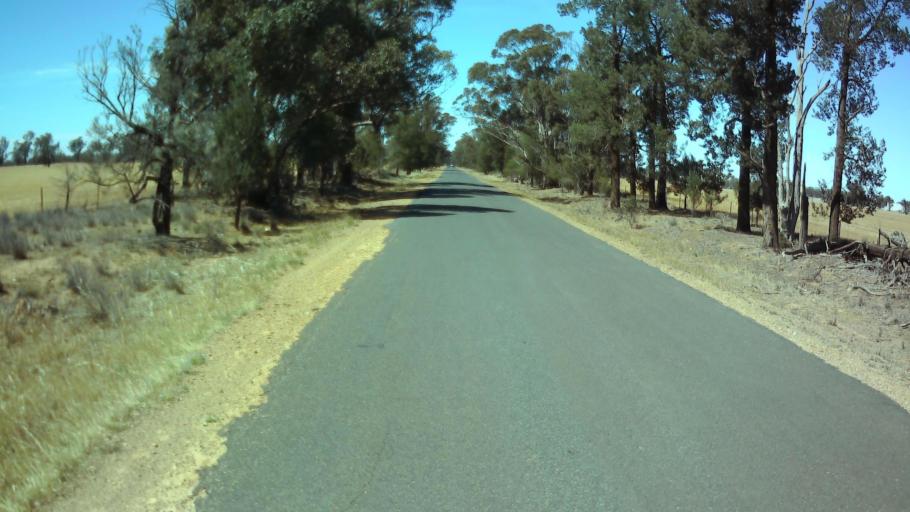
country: AU
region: New South Wales
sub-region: Weddin
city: Grenfell
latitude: -34.1087
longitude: 147.8861
